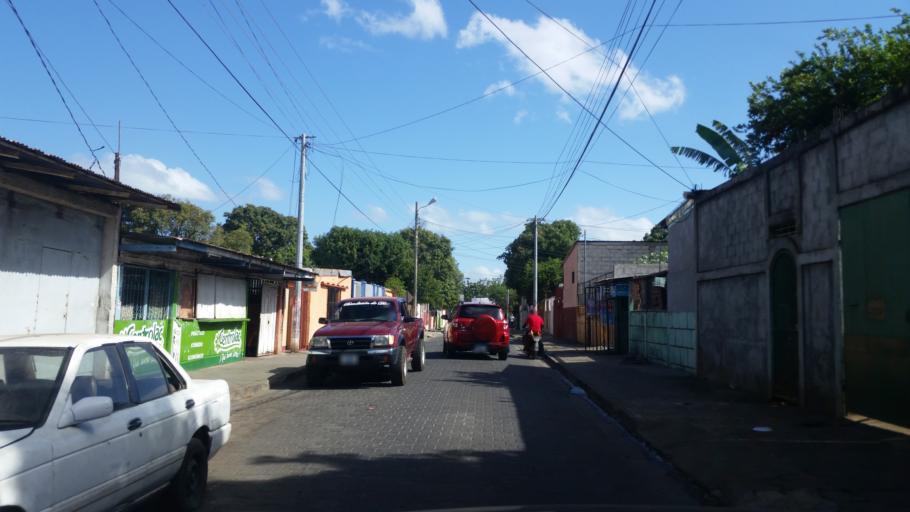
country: NI
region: Managua
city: Managua
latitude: 12.1319
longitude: -86.2370
